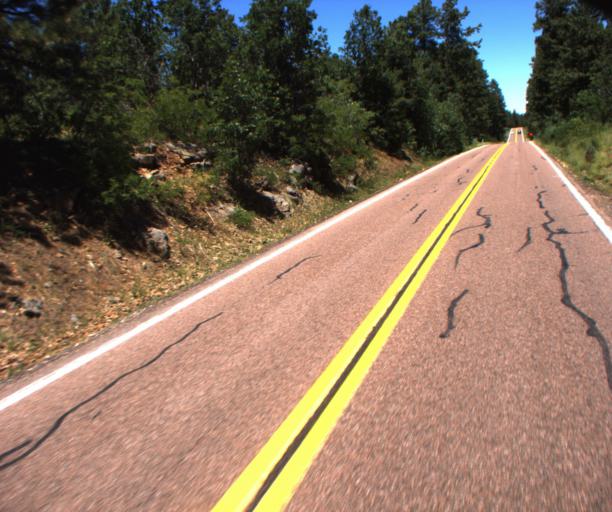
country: US
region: Arizona
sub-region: Gila County
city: Pine
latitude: 34.4760
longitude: -111.3811
